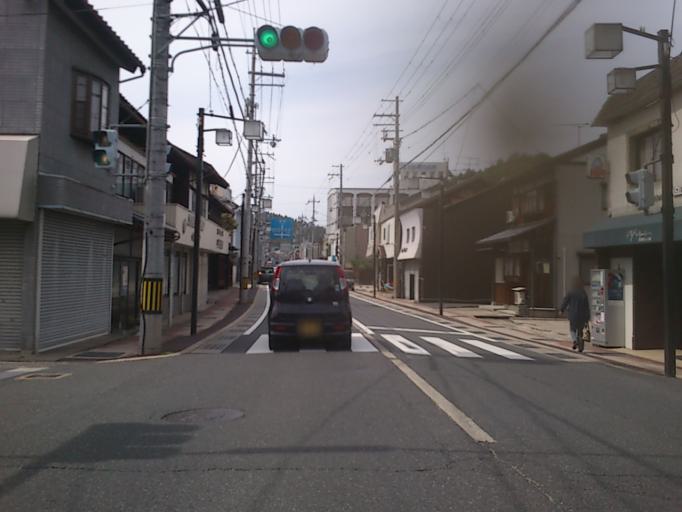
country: JP
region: Kyoto
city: Miyazu
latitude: 35.6237
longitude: 135.0586
